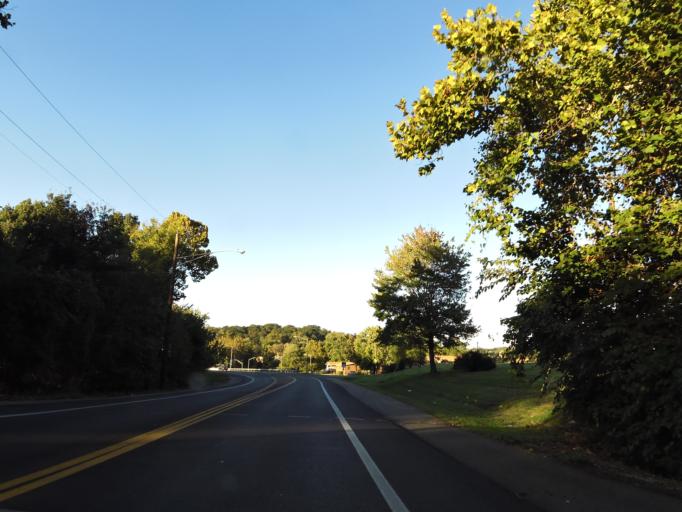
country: US
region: Tennessee
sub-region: Knox County
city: Knoxville
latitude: 36.0018
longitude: -83.9546
